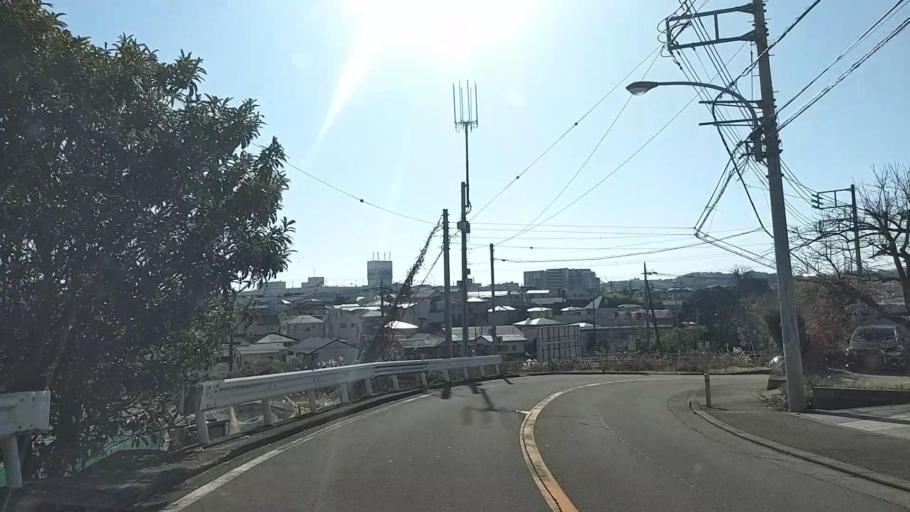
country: JP
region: Kanagawa
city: Hadano
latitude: 35.3817
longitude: 139.2269
